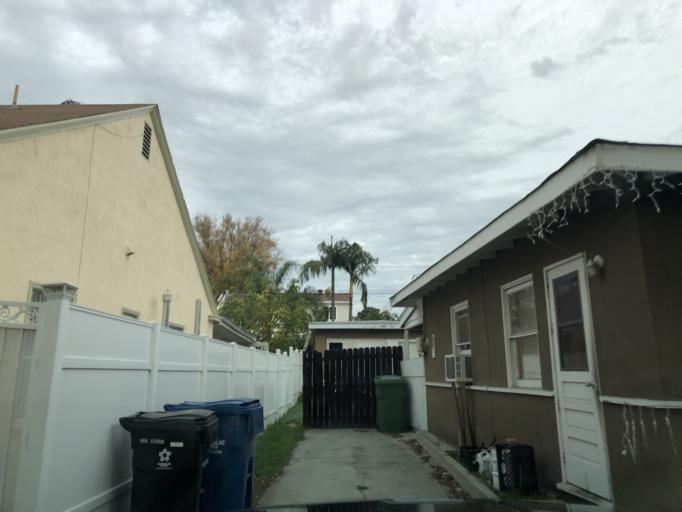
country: US
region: California
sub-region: Los Angeles County
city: South Whittier
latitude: 33.9535
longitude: -118.0222
